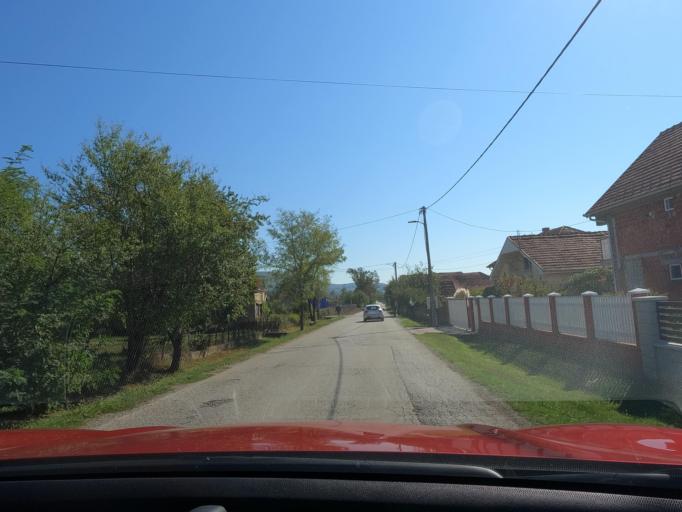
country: RS
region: Central Serbia
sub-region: Raski Okrug
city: Kraljevo
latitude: 43.7563
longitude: 20.6889
